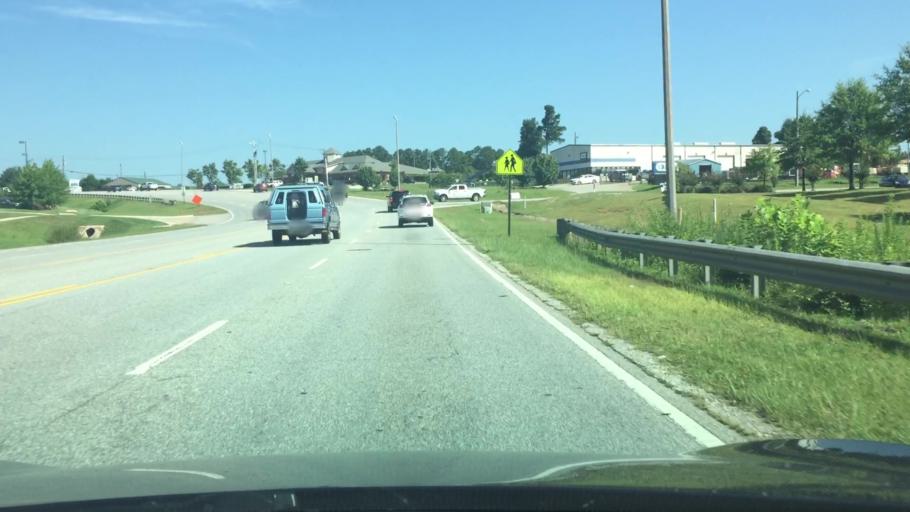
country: US
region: Alabama
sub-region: Lee County
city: Auburn
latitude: 32.6071
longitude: -85.4407
